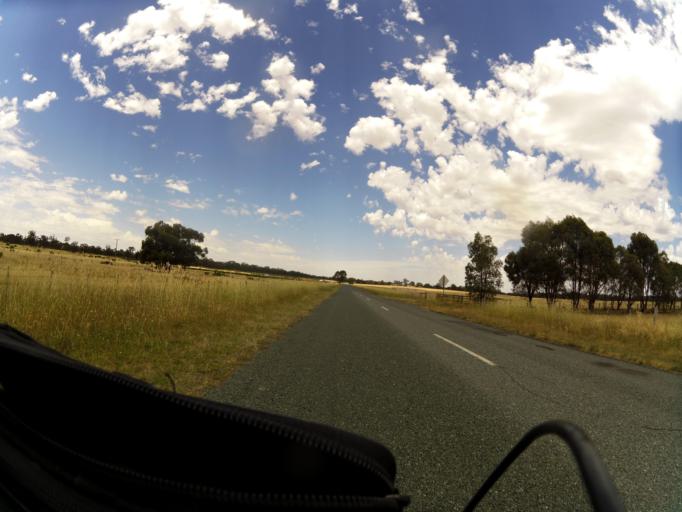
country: AU
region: Victoria
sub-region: Greater Shepparton
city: Shepparton
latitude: -36.6332
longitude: 145.2107
